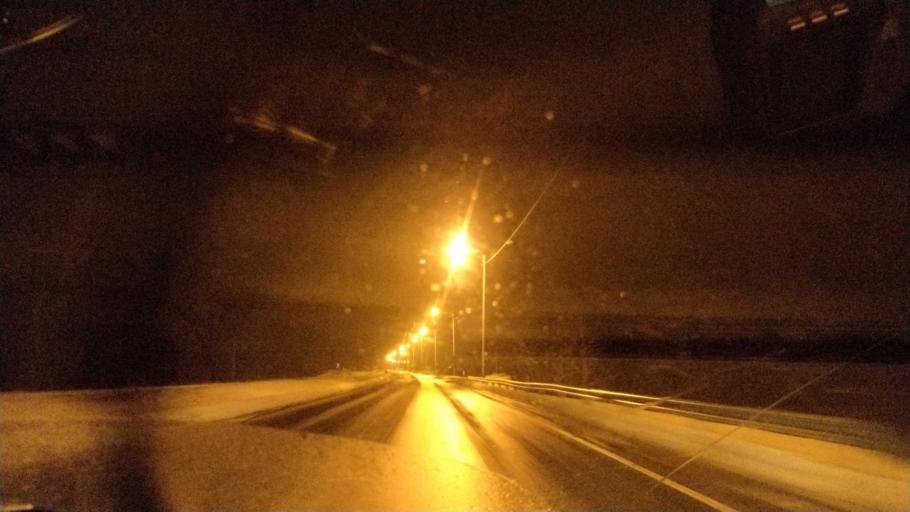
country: FI
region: Lapland
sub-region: Kemi-Tornio
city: Tervola
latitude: 66.1419
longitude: 24.9499
